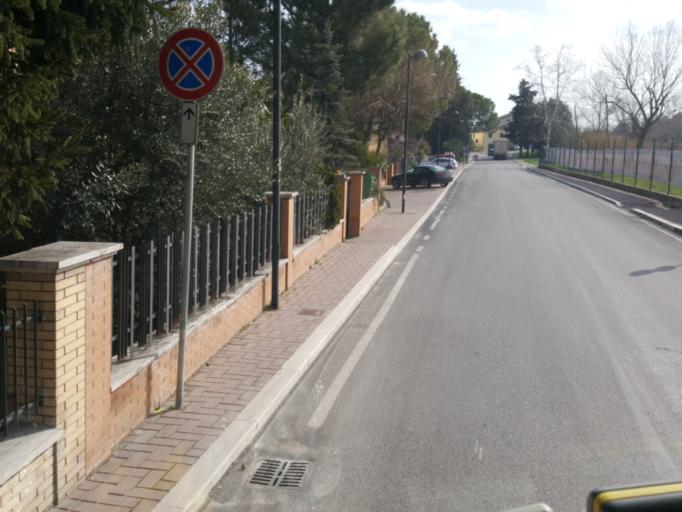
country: IT
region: The Marches
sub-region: Provincia di Macerata
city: Passo di Treia
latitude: 43.2833
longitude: 13.3308
